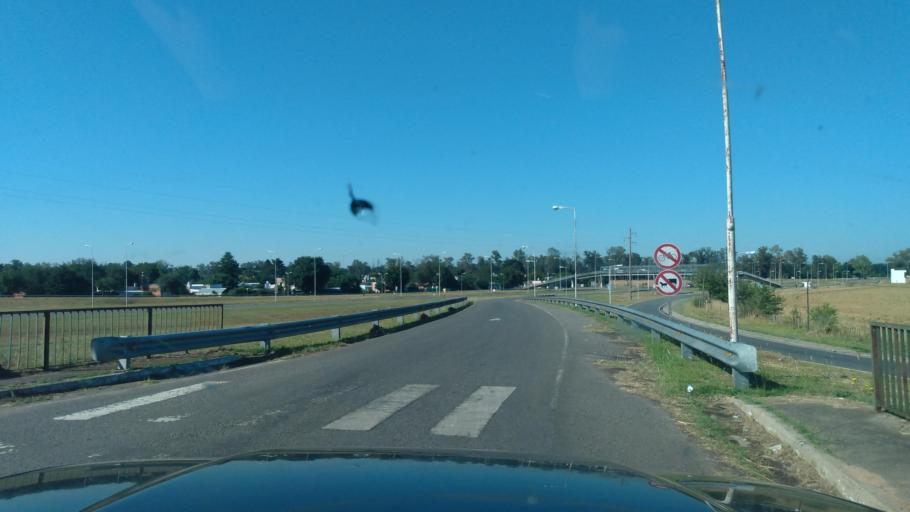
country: AR
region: Buenos Aires
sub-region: Partido de Lujan
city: Lujan
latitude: -34.6073
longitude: -59.1726
